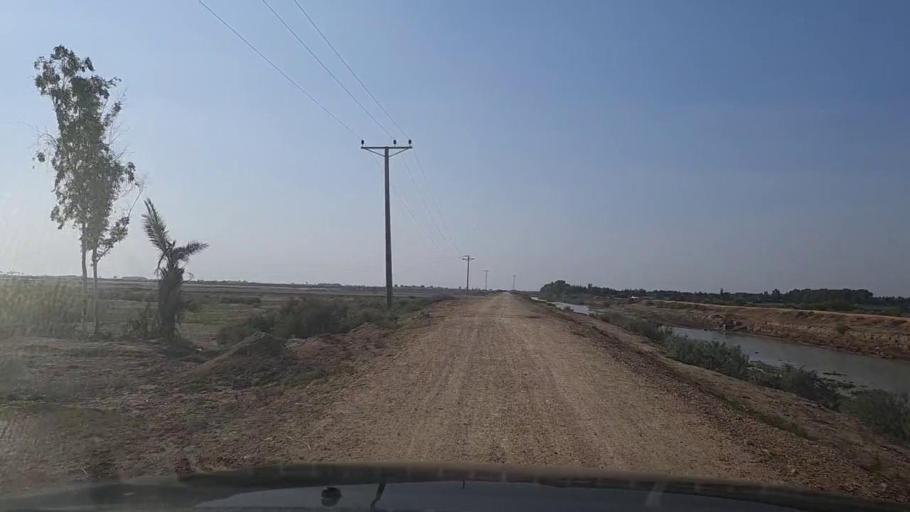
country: PK
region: Sindh
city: Thatta
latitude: 24.7111
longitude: 67.7677
